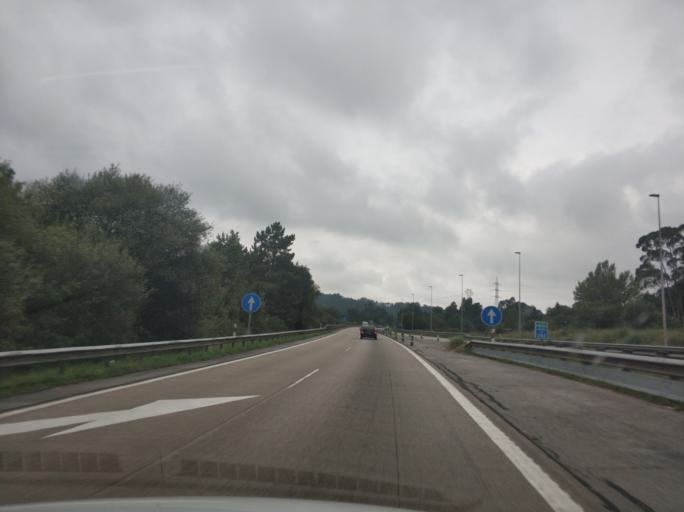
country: ES
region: Asturias
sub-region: Province of Asturias
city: Corvera de Asturias
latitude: 43.5027
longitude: -5.7927
